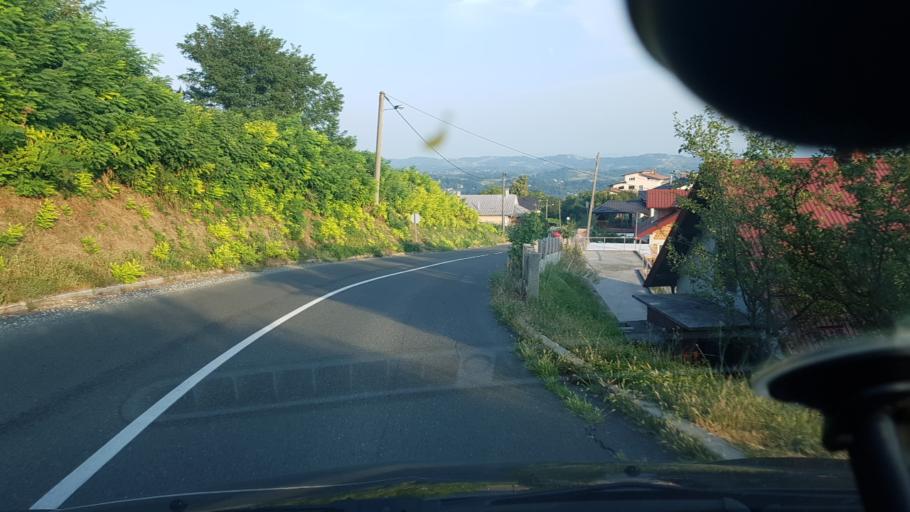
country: HR
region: Krapinsko-Zagorska
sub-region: Grad Krapina
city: Krapina
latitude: 46.1650
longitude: 15.8554
